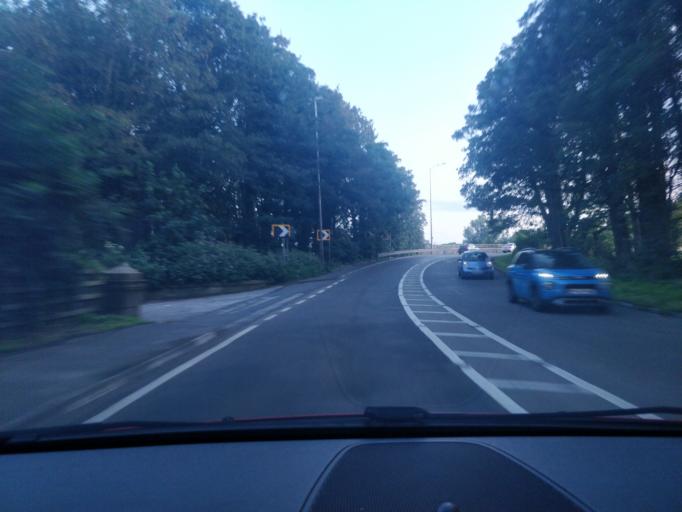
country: GB
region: England
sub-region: Lancashire
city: Tarleton
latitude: 53.6769
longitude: -2.8176
